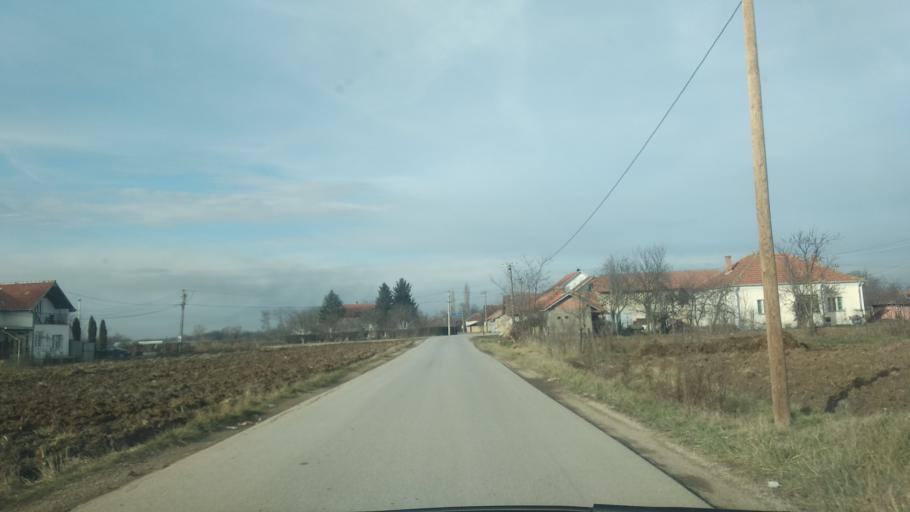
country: XK
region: Pristina
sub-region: Komuna e Gracanices
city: Glanica
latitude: 42.5941
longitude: 21.1179
